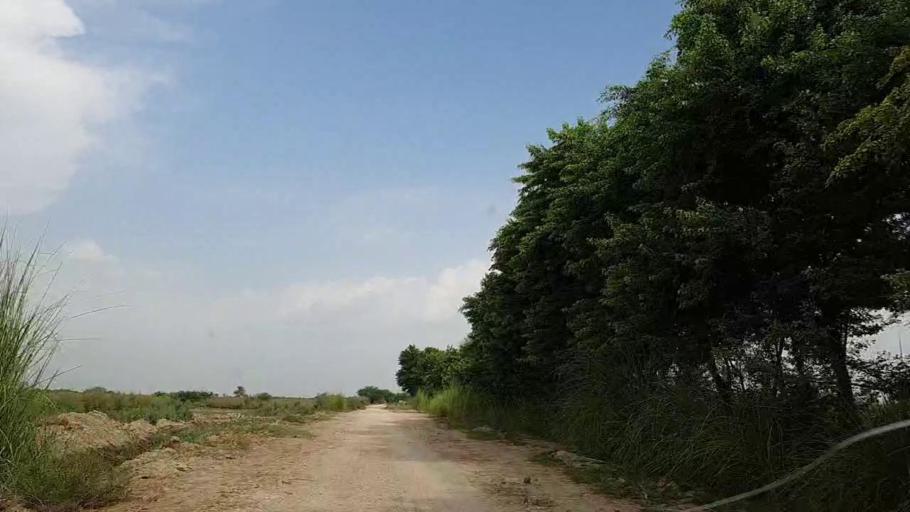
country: PK
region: Sindh
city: Khanpur
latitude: 27.8228
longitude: 69.5230
